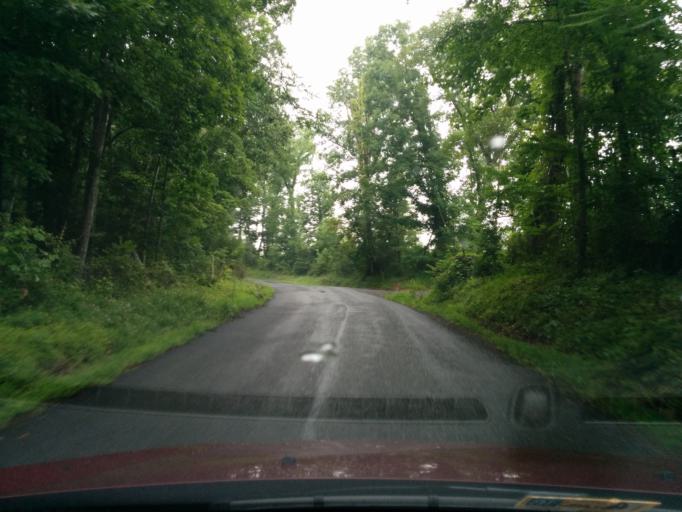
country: US
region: Virginia
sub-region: Rockbridge County
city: East Lexington
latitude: 37.8690
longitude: -79.4244
